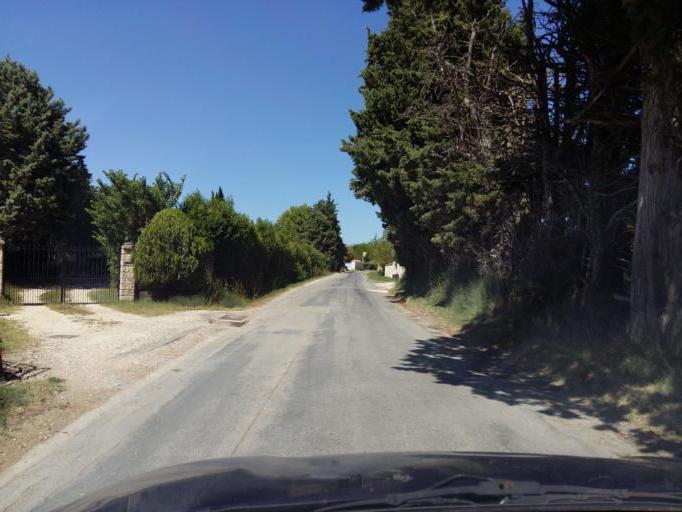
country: FR
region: Provence-Alpes-Cote d'Azur
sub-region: Departement du Vaucluse
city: Loriol-du-Comtat
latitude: 44.0796
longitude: 5.0042
